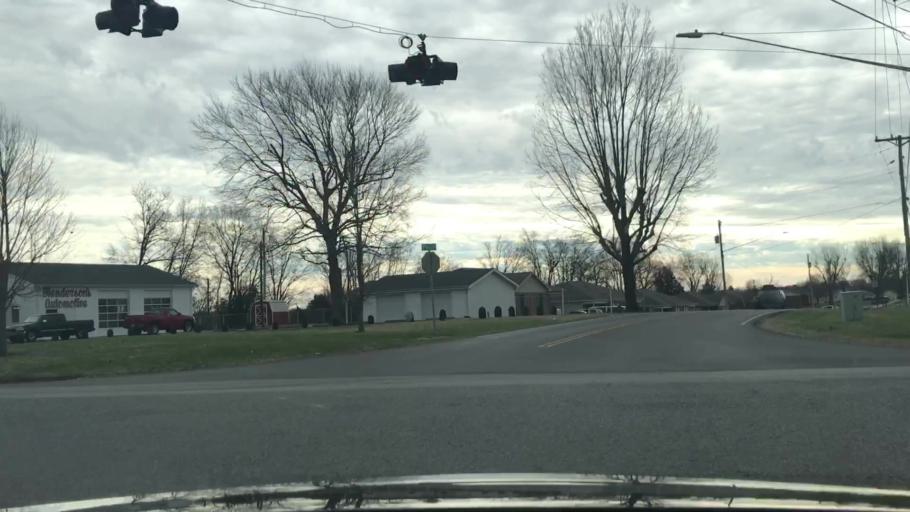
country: US
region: Kentucky
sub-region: Christian County
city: Hopkinsville
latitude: 36.8625
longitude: -87.5373
